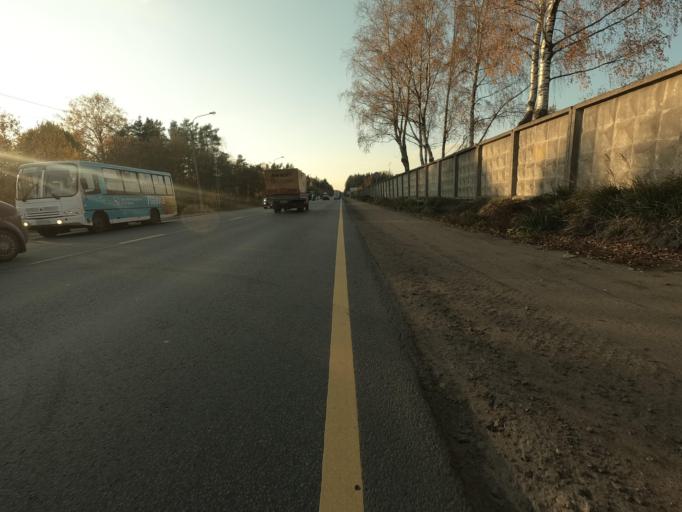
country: RU
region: St.-Petersburg
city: Pesochnyy
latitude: 60.1778
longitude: 30.1501
